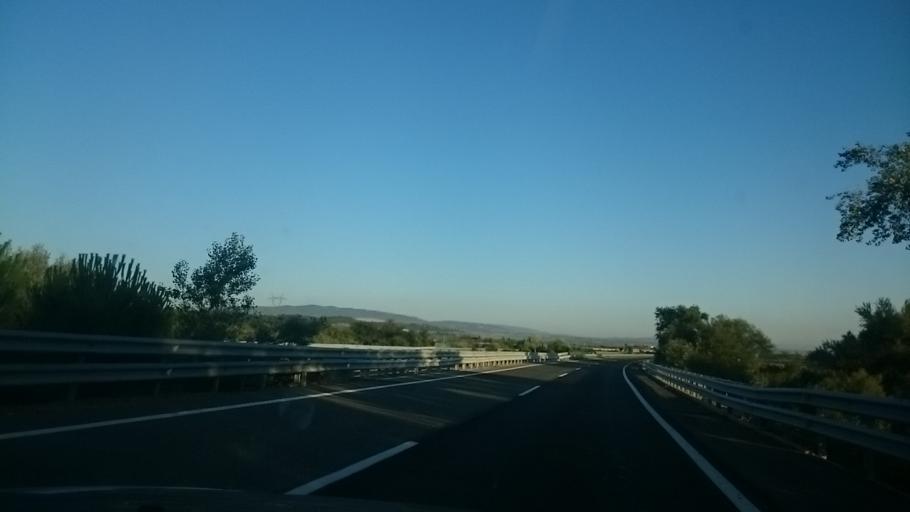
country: ES
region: Navarre
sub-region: Provincia de Navarra
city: Corella
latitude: 42.1242
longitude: -1.7512
